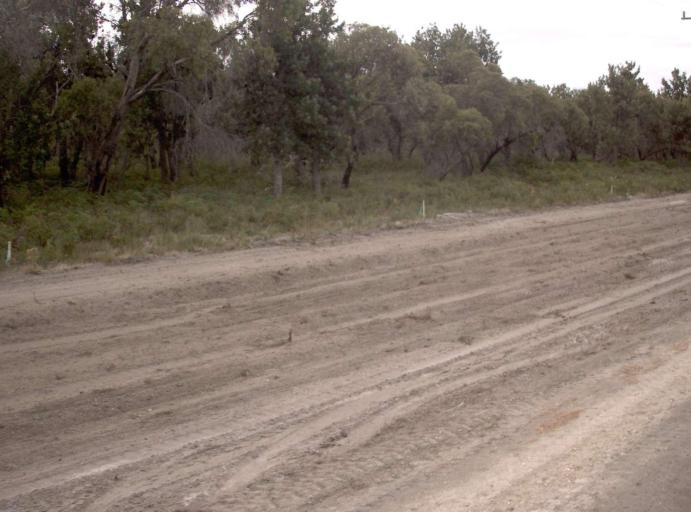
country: AU
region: Victoria
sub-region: East Gippsland
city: Bairnsdale
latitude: -38.0805
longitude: 147.5335
